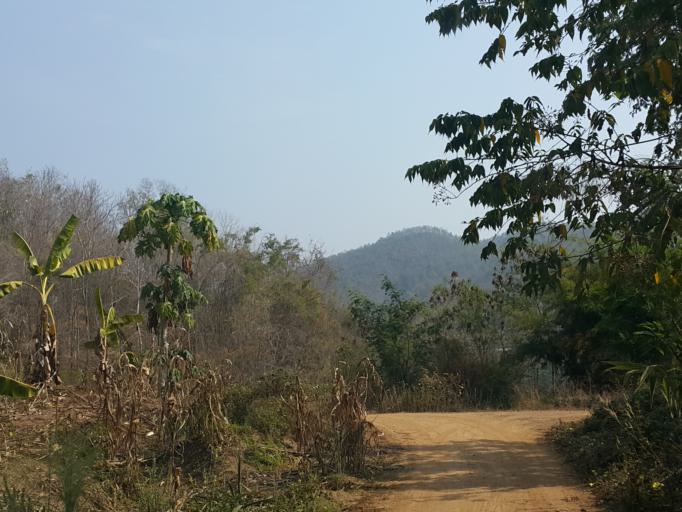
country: TH
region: Chiang Mai
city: Hang Dong
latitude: 18.7360
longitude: 98.8599
